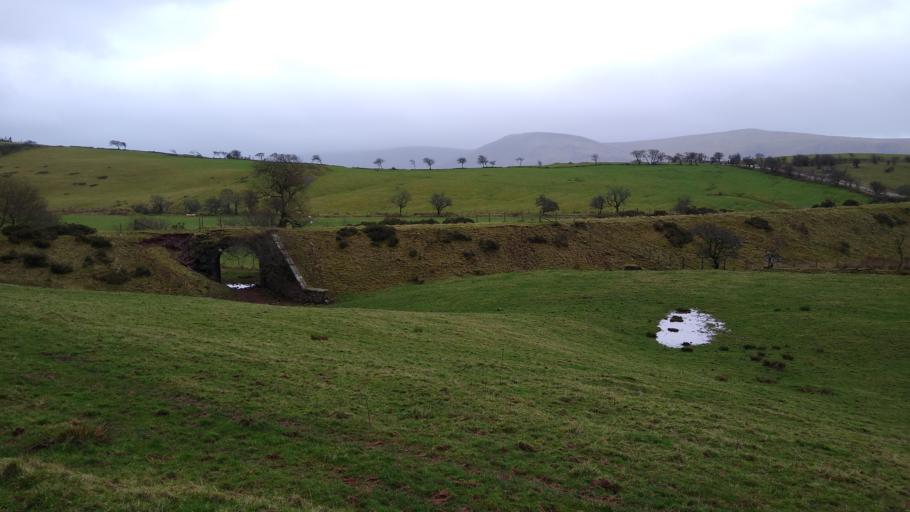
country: GB
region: England
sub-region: Cumbria
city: Frizington
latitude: 54.5537
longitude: -3.4128
